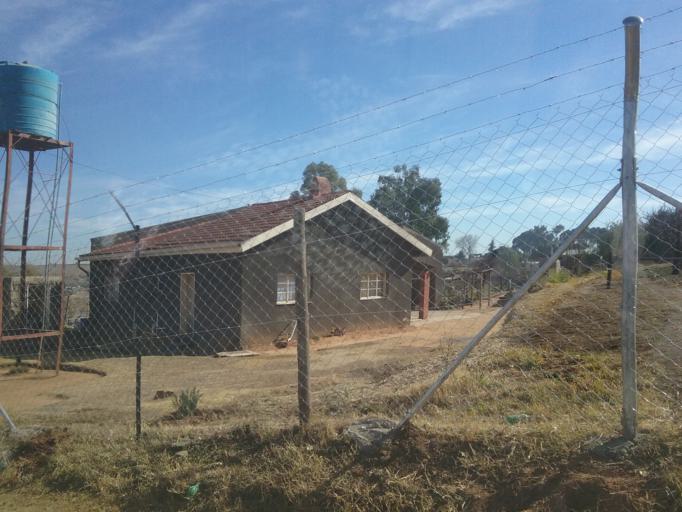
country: LS
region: Maseru
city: Maseru
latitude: -29.4181
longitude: 27.5567
